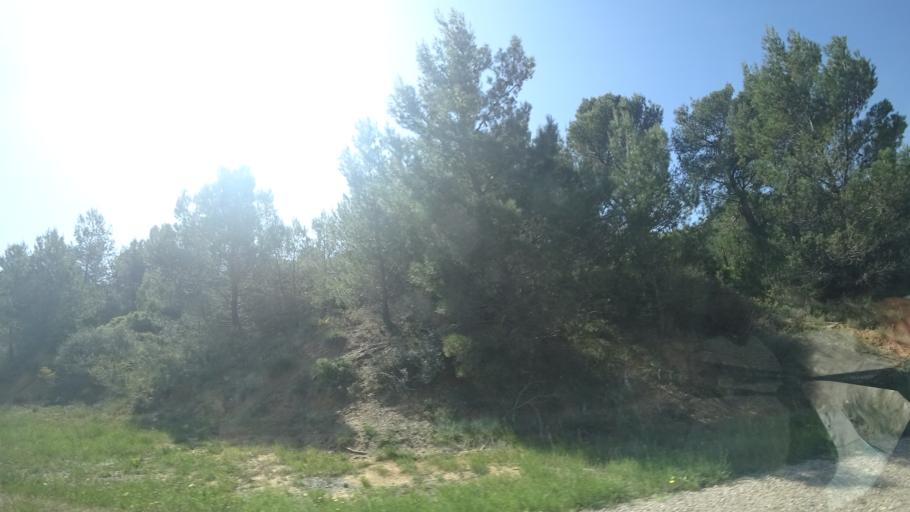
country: FR
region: Languedoc-Roussillon
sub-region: Departement de l'Herault
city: Olonzac
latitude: 43.3396
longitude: 2.7344
